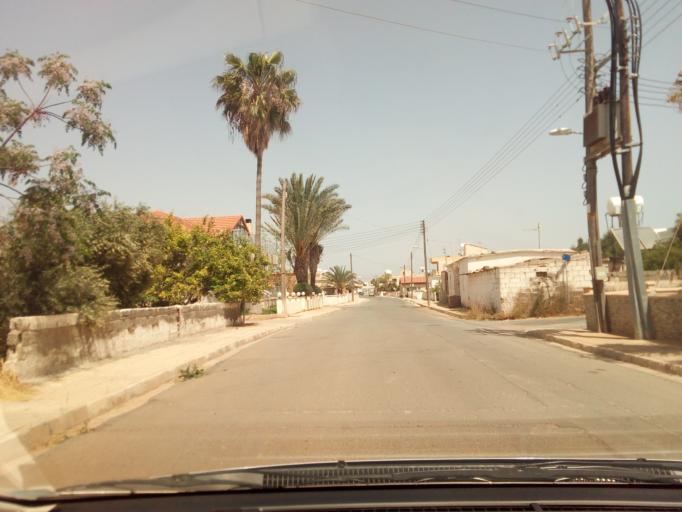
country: CY
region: Ammochostos
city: Liopetri
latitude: 34.9729
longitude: 33.8491
